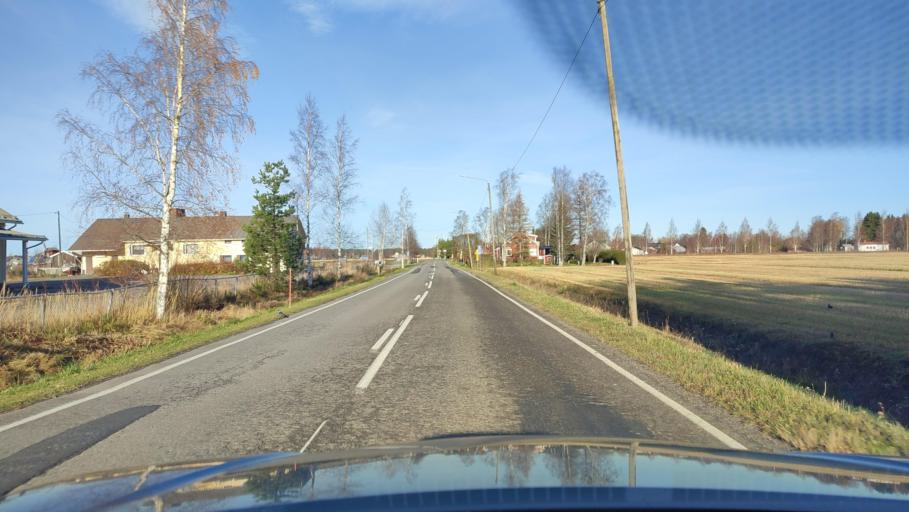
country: FI
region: Southern Ostrobothnia
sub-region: Suupohja
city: Teuva
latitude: 62.4669
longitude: 21.7136
